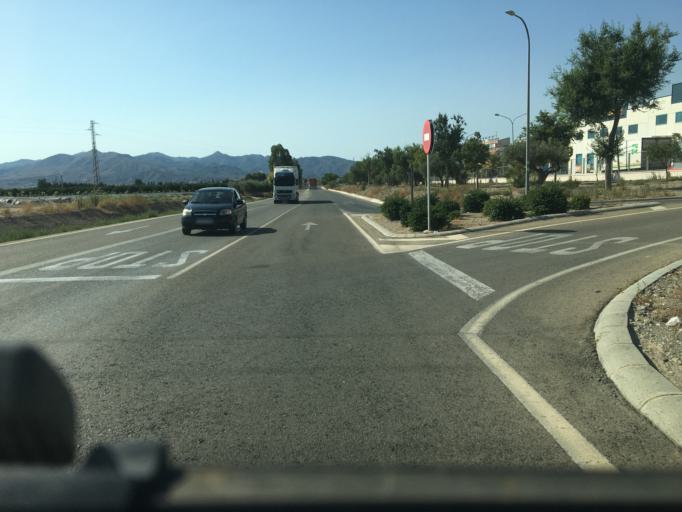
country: ES
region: Andalusia
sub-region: Provincia de Almeria
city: Huercal-Overa
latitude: 37.4157
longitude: -1.9660
